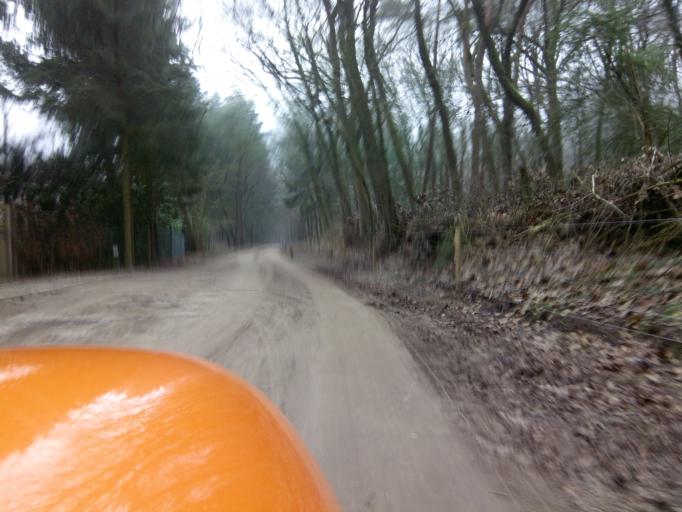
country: NL
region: Gelderland
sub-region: Gemeente Barneveld
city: Garderen
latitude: 52.2192
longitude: 5.6841
